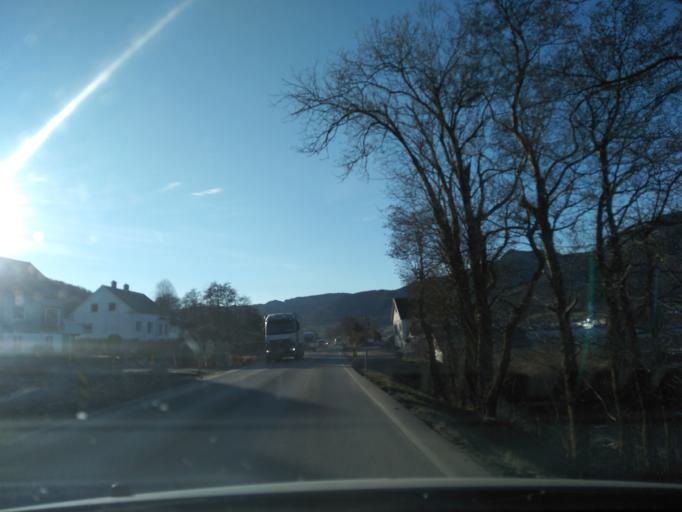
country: NO
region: Rogaland
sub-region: Vindafjord
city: Olen
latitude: 59.6025
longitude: 5.7923
